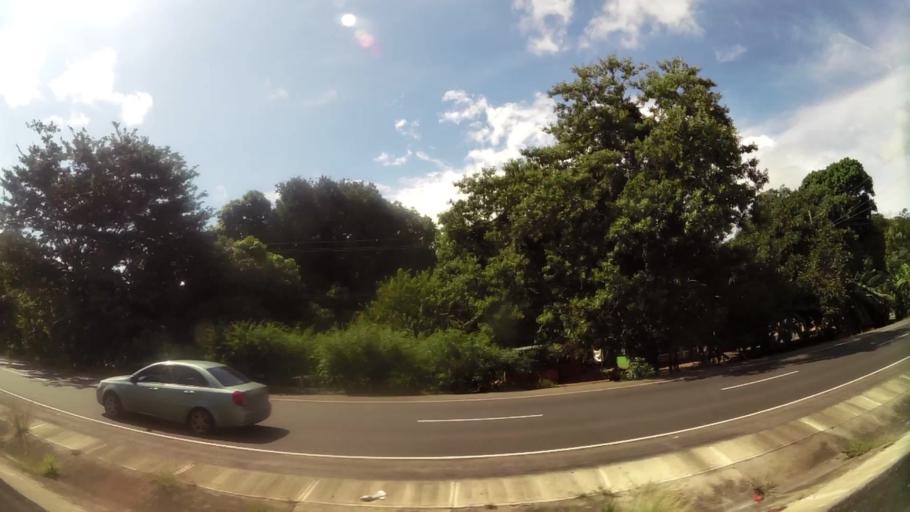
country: PA
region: Panama
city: Bejuco
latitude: 8.6374
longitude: -79.8806
